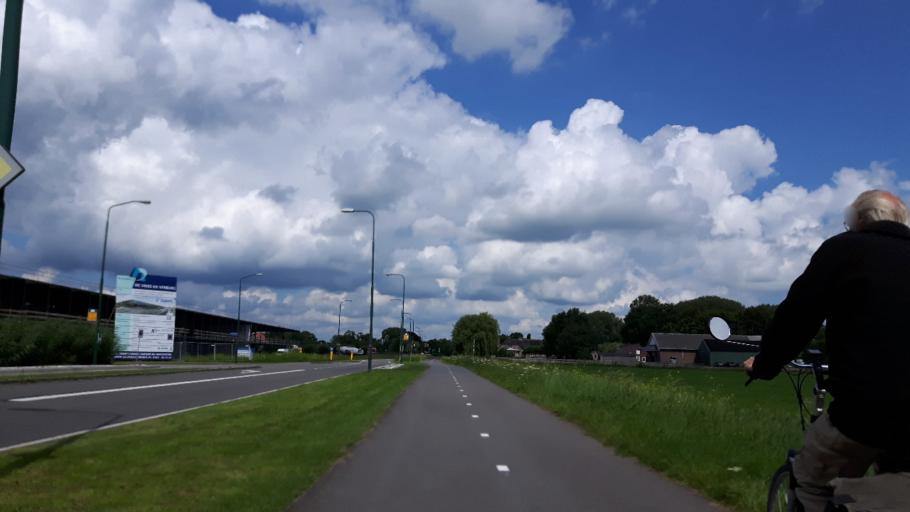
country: NL
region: Utrecht
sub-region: Gemeente Woerden
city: Woerden
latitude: 52.0938
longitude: 4.9122
